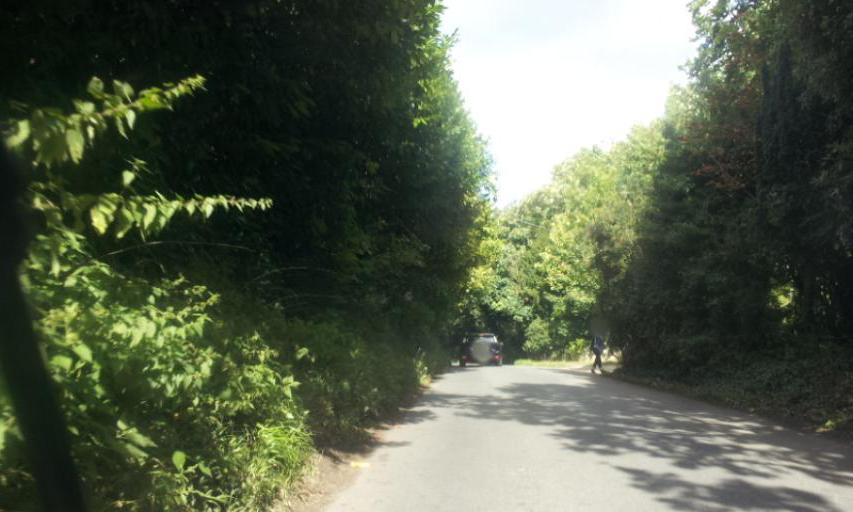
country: GB
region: England
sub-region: Kent
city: West Malling
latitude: 51.3203
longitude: 0.4100
